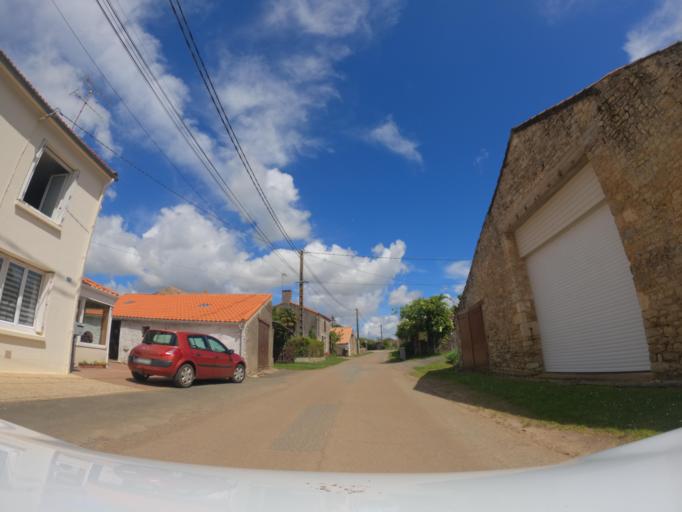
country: FR
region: Pays de la Loire
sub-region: Departement de la Vendee
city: Le Champ-Saint-Pere
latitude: 46.4896
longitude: -1.3230
